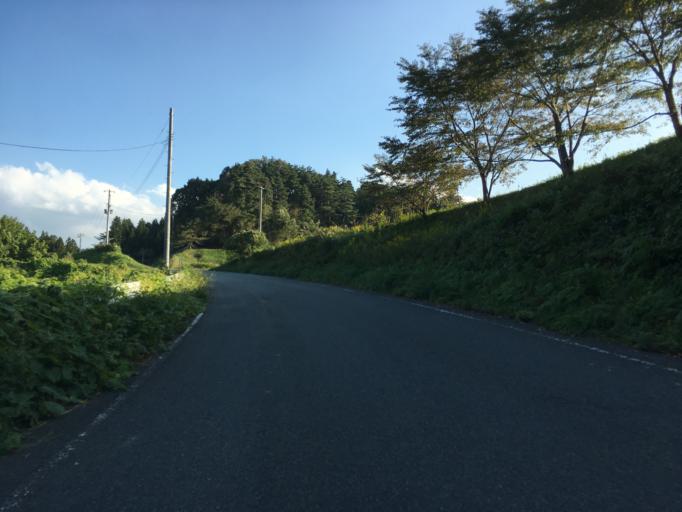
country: JP
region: Fukushima
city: Fukushima-shi
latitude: 37.6474
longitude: 140.5494
